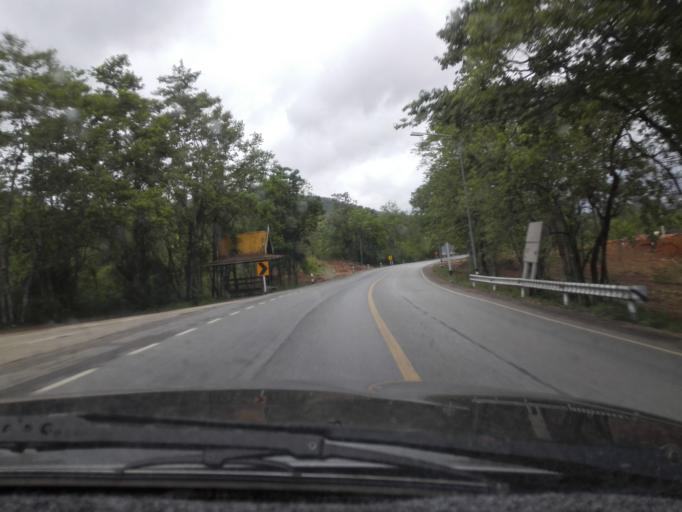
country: TH
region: Tak
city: Tak
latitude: 16.7910
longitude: 99.0151
